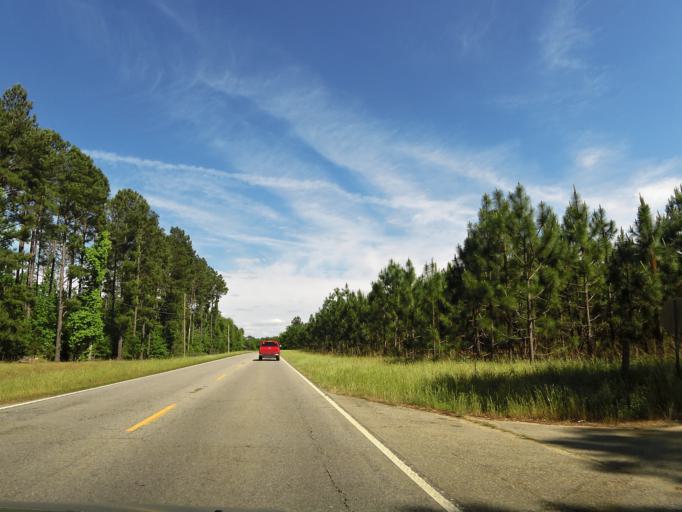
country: US
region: South Carolina
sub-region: Bamberg County
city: Denmark
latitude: 33.3356
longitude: -81.1642
